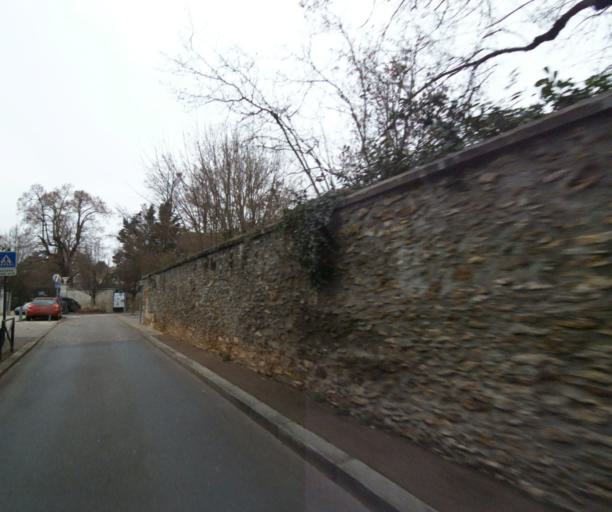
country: FR
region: Ile-de-France
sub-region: Departement des Hauts-de-Seine
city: Vaucresson
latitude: 48.8392
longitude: 2.1593
